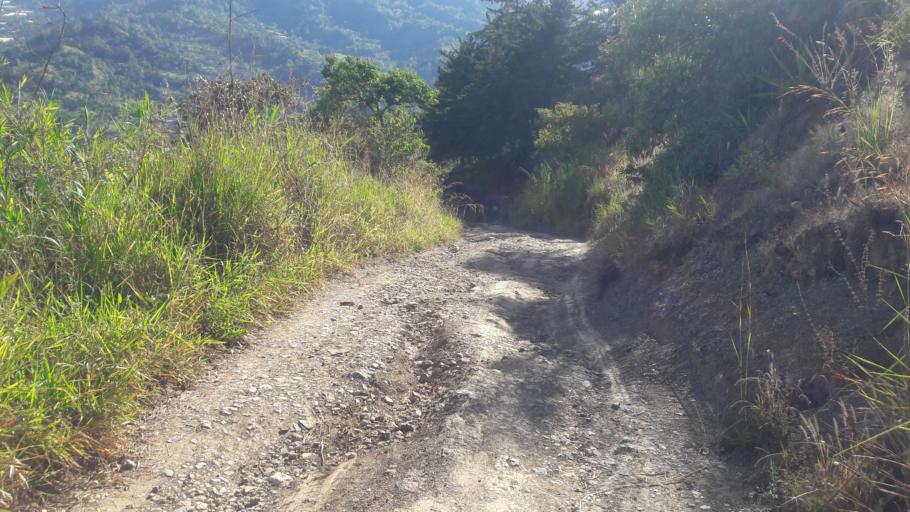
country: CO
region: Cundinamarca
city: Tenza
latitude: 5.0868
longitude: -73.4152
